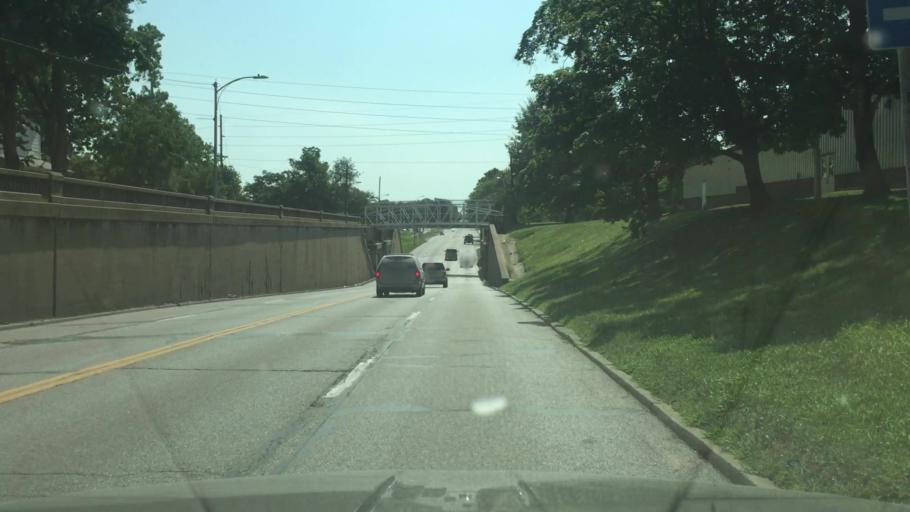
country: US
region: Missouri
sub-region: Pettis County
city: Sedalia
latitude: 38.7040
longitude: -93.2247
